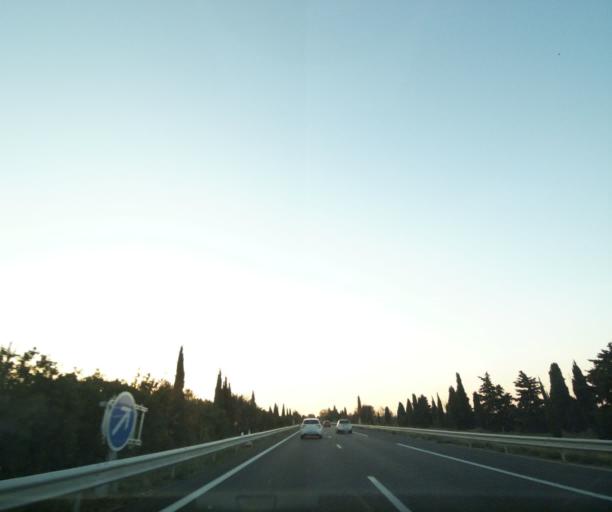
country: FR
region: Provence-Alpes-Cote d'Azur
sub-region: Departement des Bouches-du-Rhone
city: Mouries
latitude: 43.6392
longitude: 4.8817
